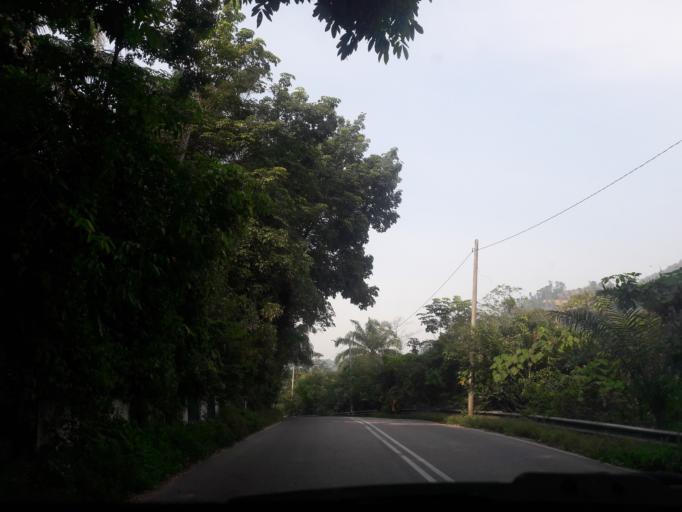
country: MY
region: Kedah
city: Kulim
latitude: 5.3689
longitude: 100.5226
